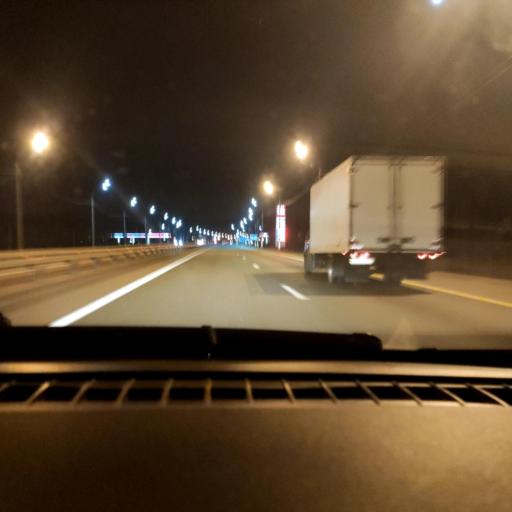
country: RU
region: Lipetsk
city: Khlevnoye
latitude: 52.2199
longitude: 39.1270
